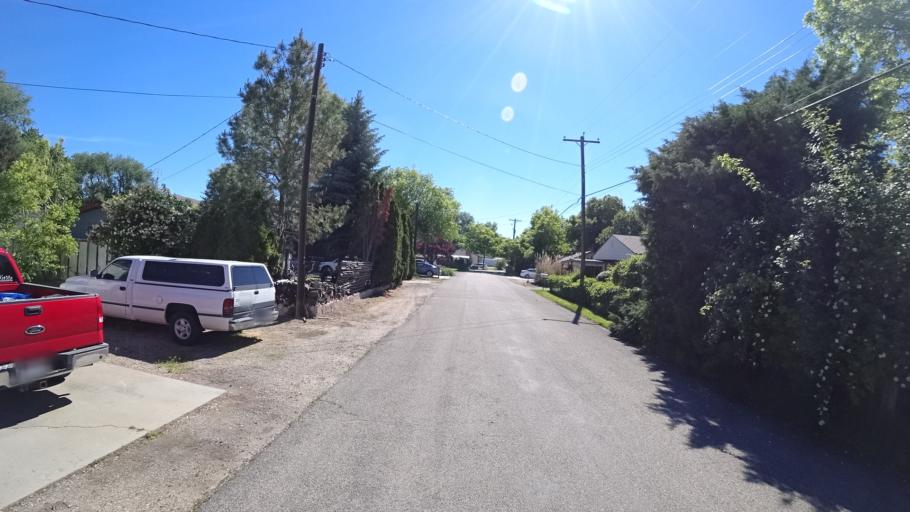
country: US
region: Idaho
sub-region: Ada County
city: Garden City
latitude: 43.6469
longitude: -116.2317
